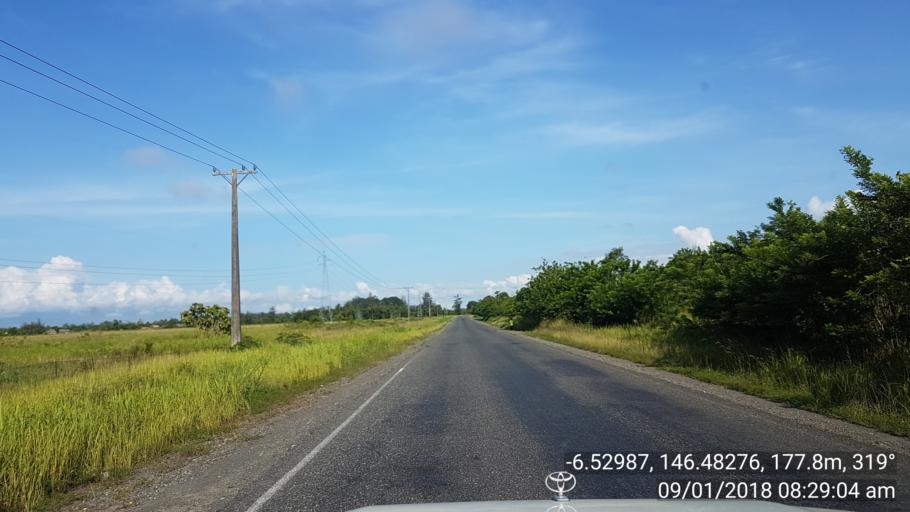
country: PG
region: Morobe
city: Lae
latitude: -6.5301
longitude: 146.4828
